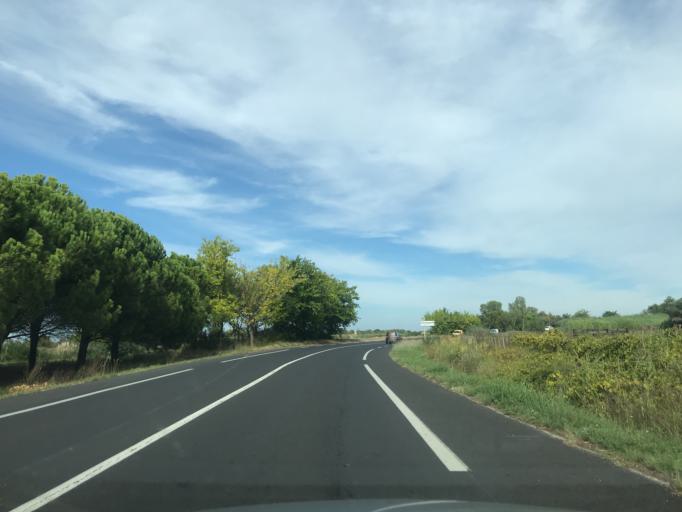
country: FR
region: Languedoc-Roussillon
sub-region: Departement du Gard
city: Aigues-Mortes
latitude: 43.5869
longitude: 4.2122
